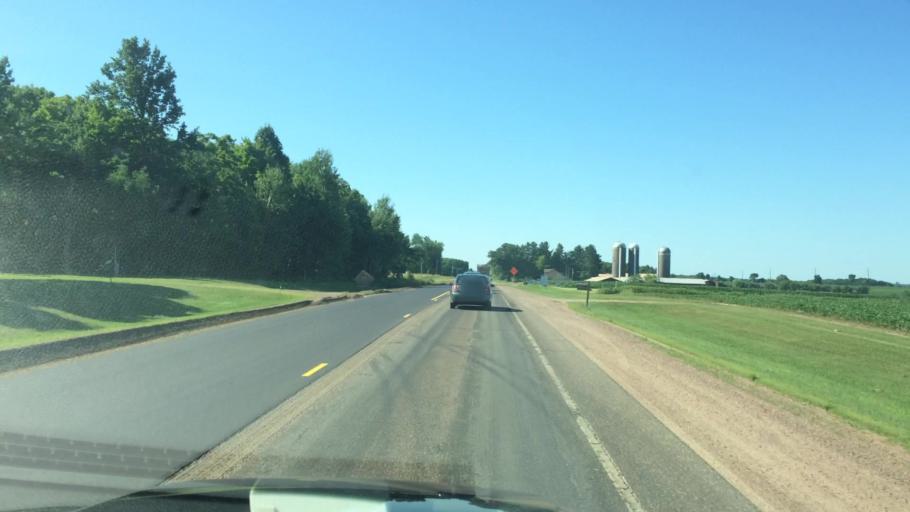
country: US
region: Wisconsin
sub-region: Marathon County
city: Stratford
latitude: 44.8670
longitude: -90.0791
